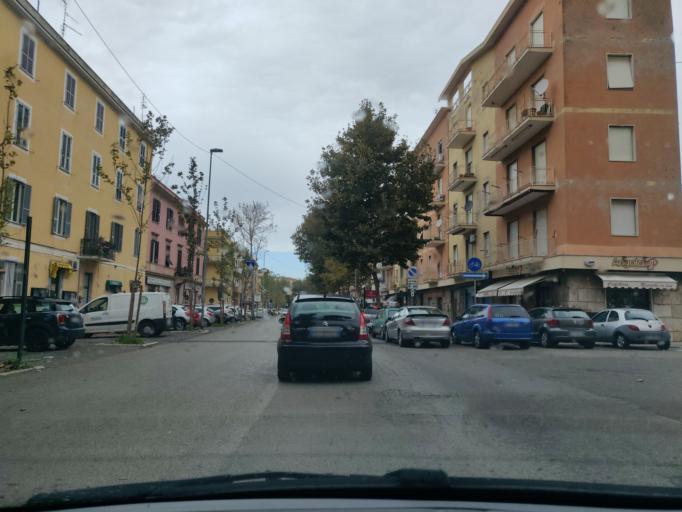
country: IT
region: Latium
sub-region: Citta metropolitana di Roma Capitale
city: Civitavecchia
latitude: 42.0924
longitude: 11.7996
